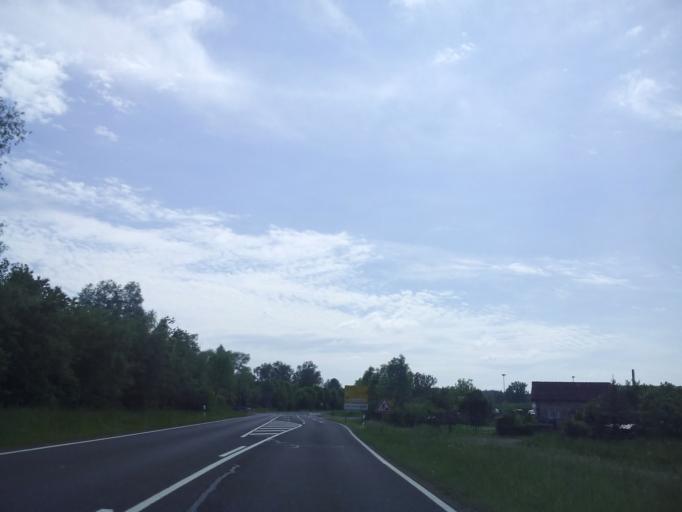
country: DE
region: Thuringia
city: Hellingen
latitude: 50.2760
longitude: 10.7296
